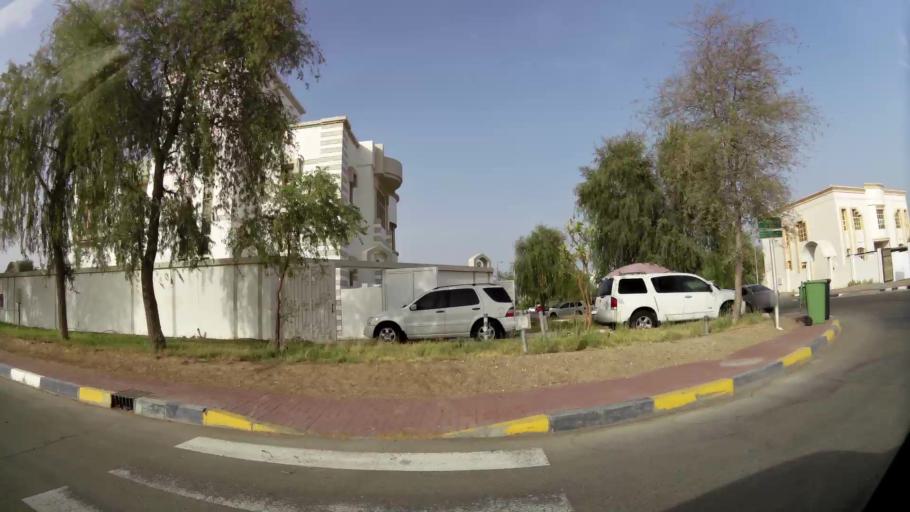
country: AE
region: Abu Dhabi
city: Al Ain
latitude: 24.2263
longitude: 55.6671
